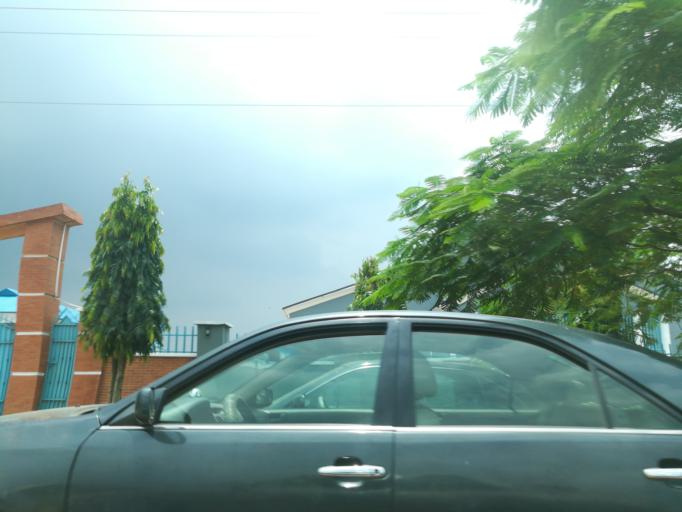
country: NG
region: Lagos
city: Ikorodu
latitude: 6.6096
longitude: 3.5824
